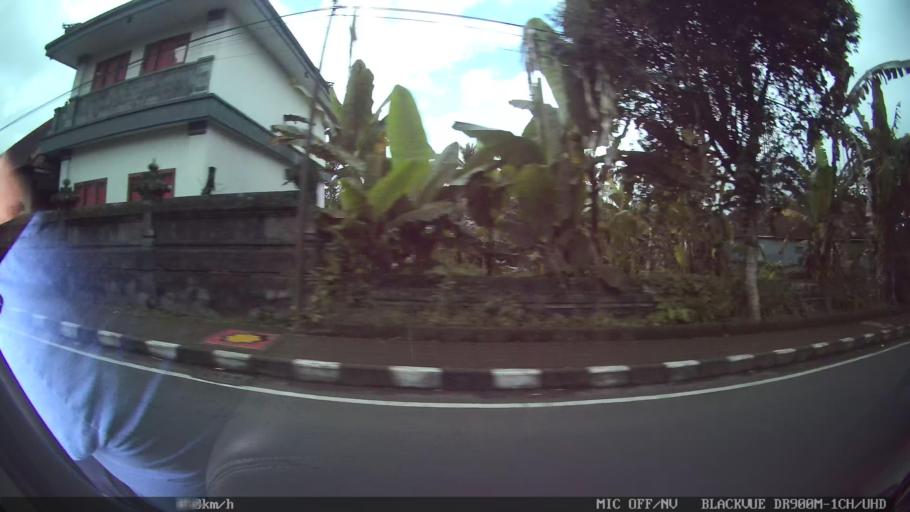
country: ID
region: Bali
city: Petang
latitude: -8.3901
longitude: 115.2194
